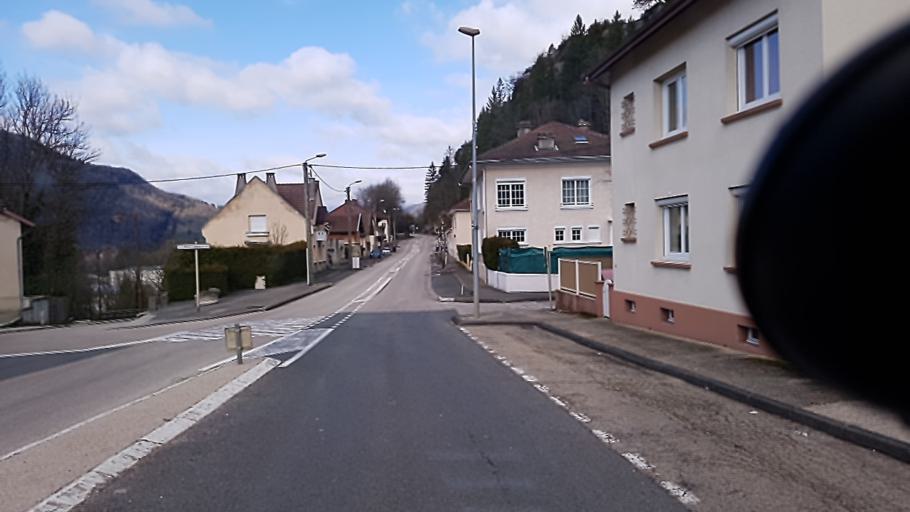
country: FR
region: Rhone-Alpes
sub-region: Departement de l'Ain
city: Dortan
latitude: 46.3190
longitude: 5.6604
